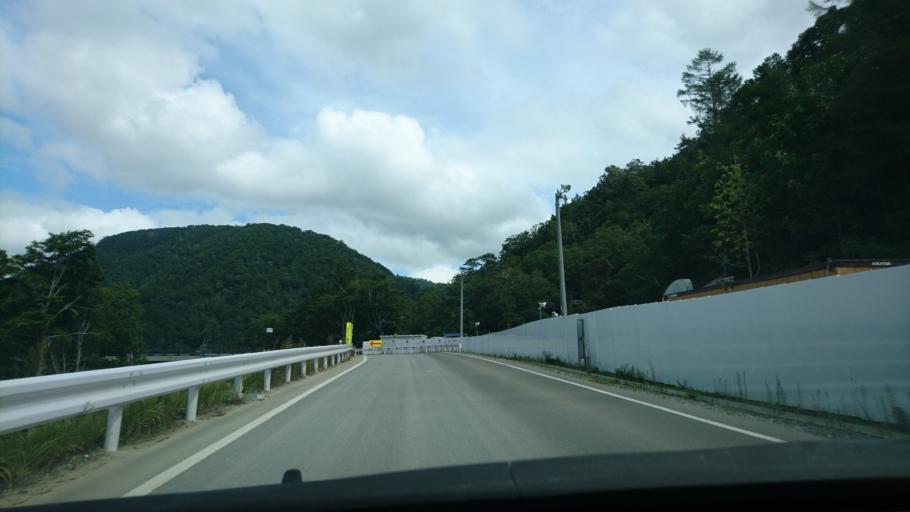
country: JP
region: Akita
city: Yuzawa
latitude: 39.0357
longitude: 140.7343
